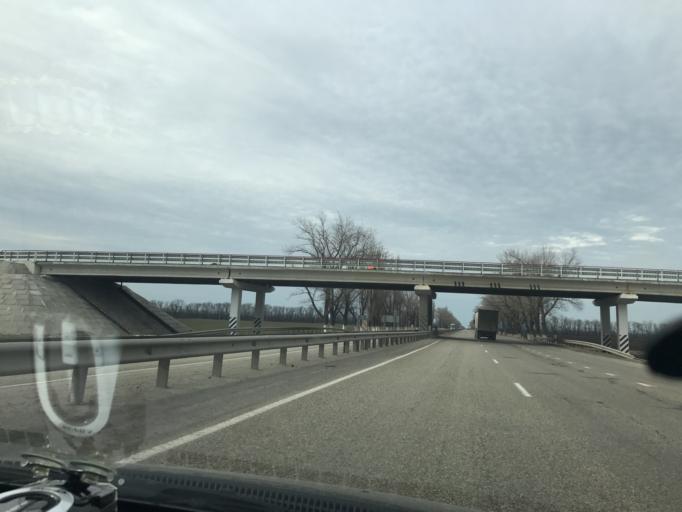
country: RU
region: Krasnodarskiy
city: Novokubansk
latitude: 45.0586
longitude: 40.9848
